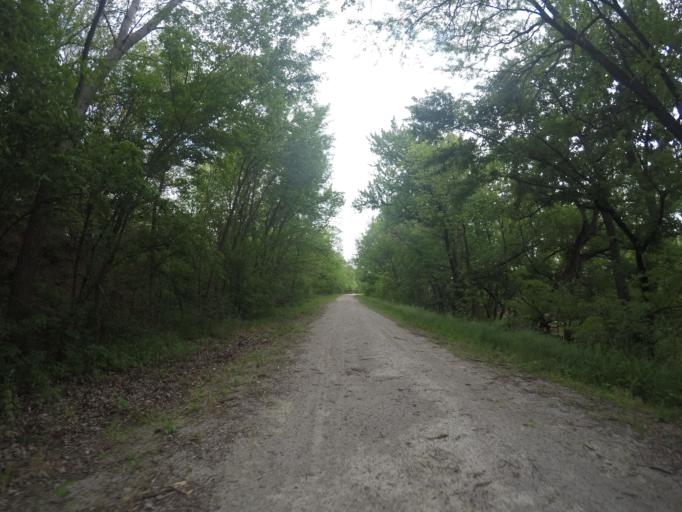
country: US
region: Nebraska
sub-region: Gage County
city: Wymore
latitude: 39.9979
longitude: -96.5936
